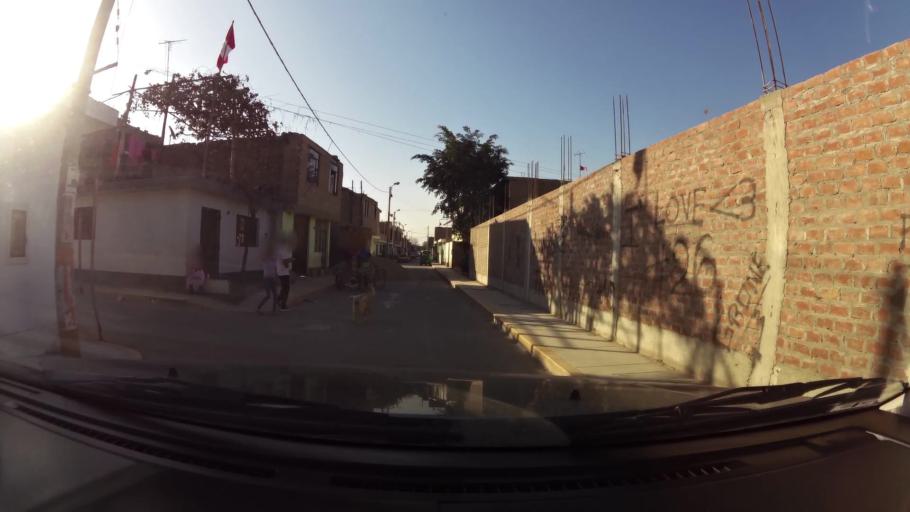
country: PE
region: Ica
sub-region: Provincia de Ica
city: Ica
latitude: -14.0659
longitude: -75.7180
